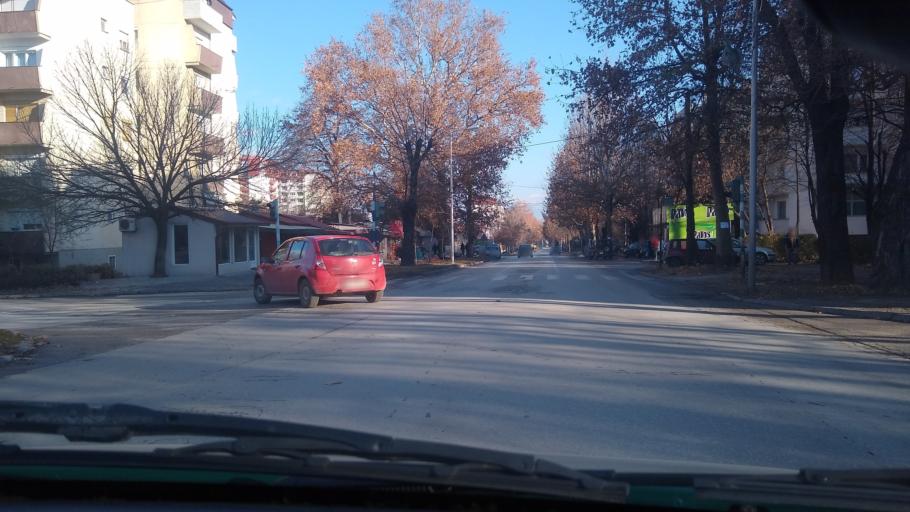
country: MK
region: Bitola
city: Bitola
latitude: 41.0238
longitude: 21.3241
